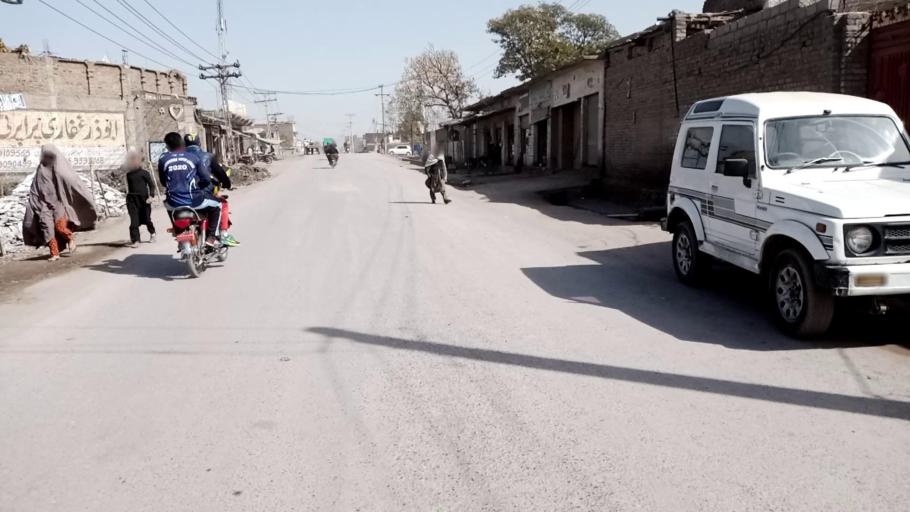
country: PK
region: Khyber Pakhtunkhwa
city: Peshawar
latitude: 34.0033
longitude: 71.6388
